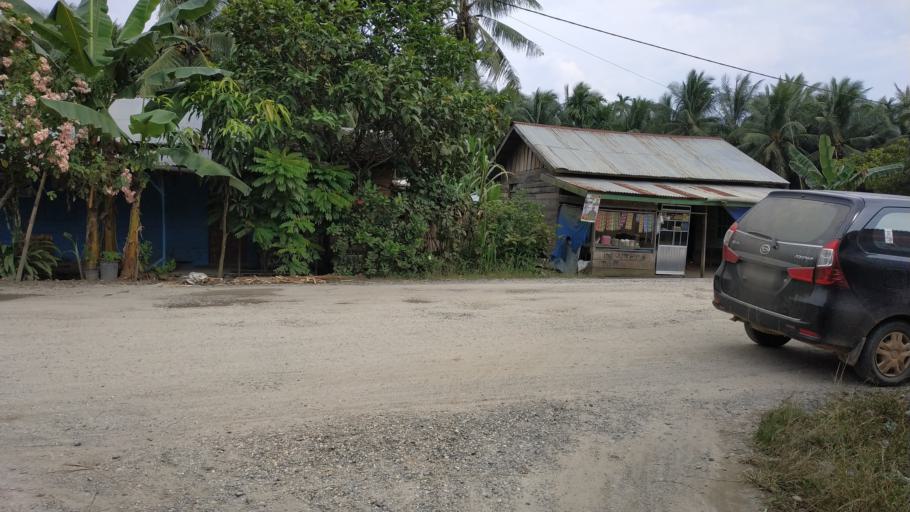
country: ID
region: Riau
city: Sungaisalak
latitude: -0.5174
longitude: 103.0041
